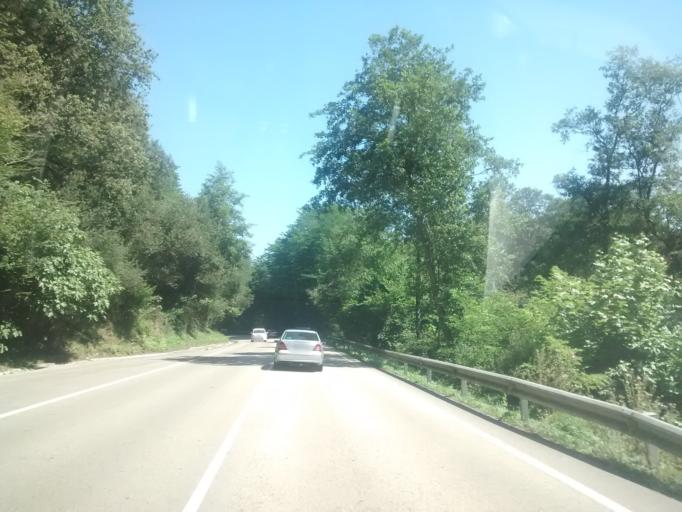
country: ES
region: Cantabria
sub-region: Provincia de Cantabria
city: Hazas de Cesto
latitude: 43.4279
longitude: -3.5677
